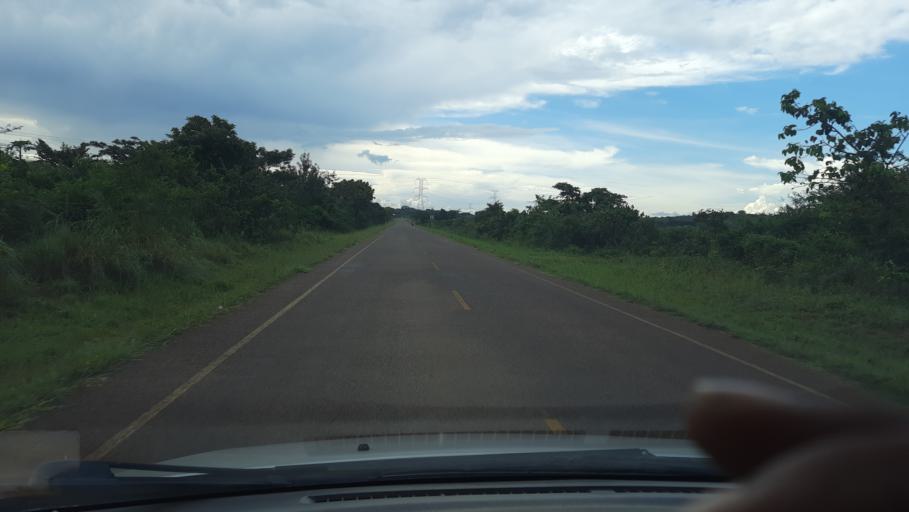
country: UG
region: Central Region
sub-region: Nakasongola District
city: Nakasongola
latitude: 1.3206
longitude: 32.4330
